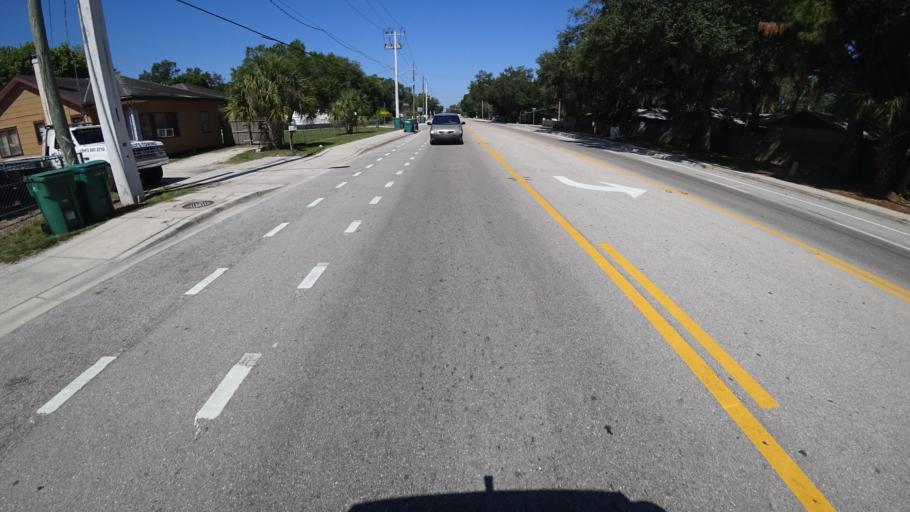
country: US
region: Florida
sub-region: Manatee County
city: West Samoset
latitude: 27.4402
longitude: -82.5559
